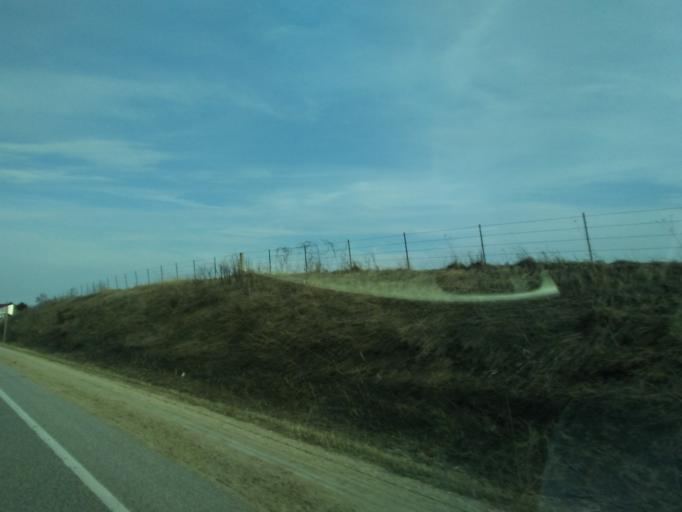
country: US
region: Wisconsin
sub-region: Grant County
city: Fennimore
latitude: 42.9738
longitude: -90.6051
